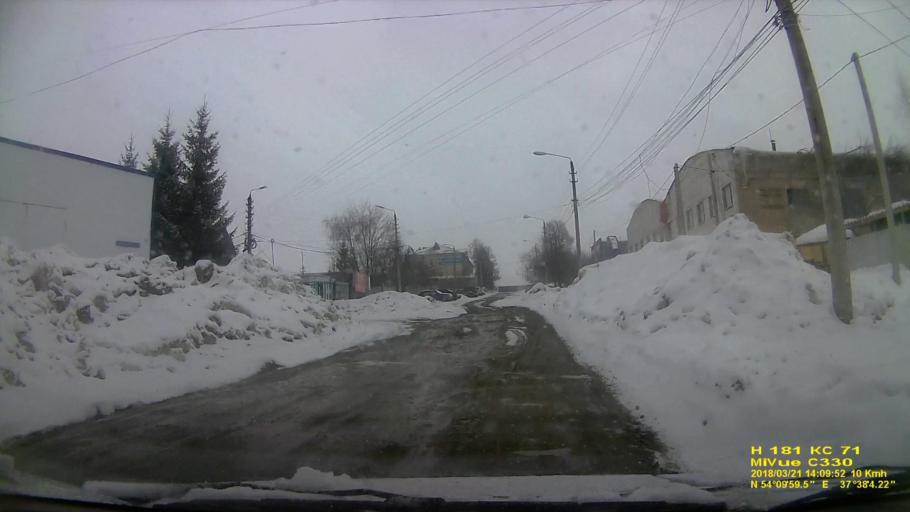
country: RU
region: Tula
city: Tula
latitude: 54.1665
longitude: 37.6346
